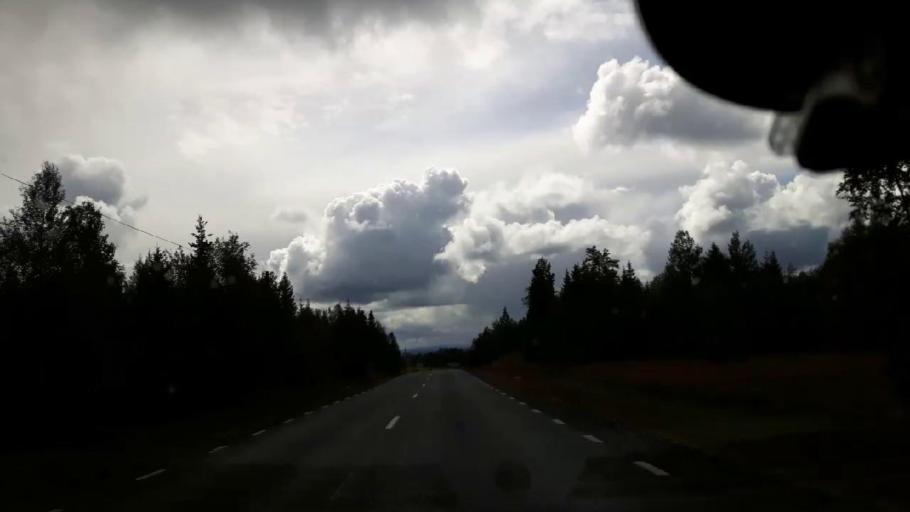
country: SE
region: Jaemtland
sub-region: Krokoms Kommun
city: Valla
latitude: 63.4286
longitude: 13.8019
